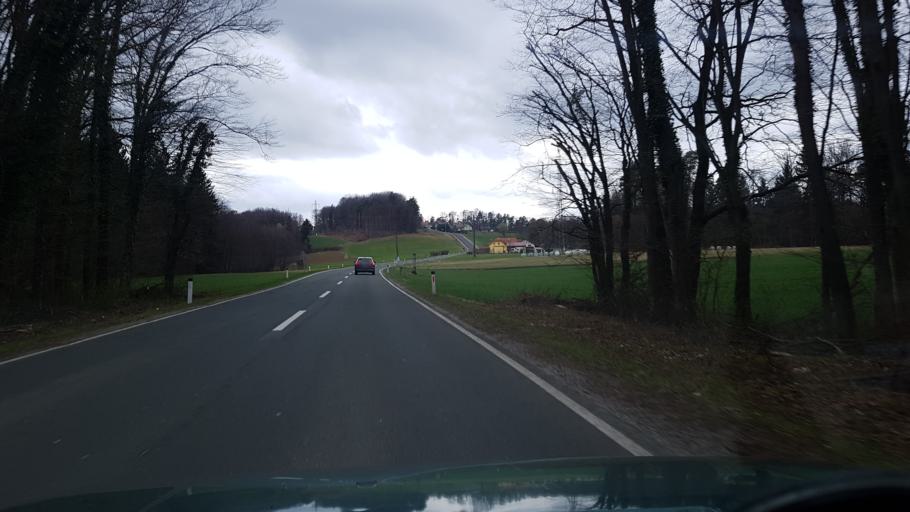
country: SI
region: Slovenska Bistrica
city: Slovenska Bistrica
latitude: 46.3733
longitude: 15.5359
